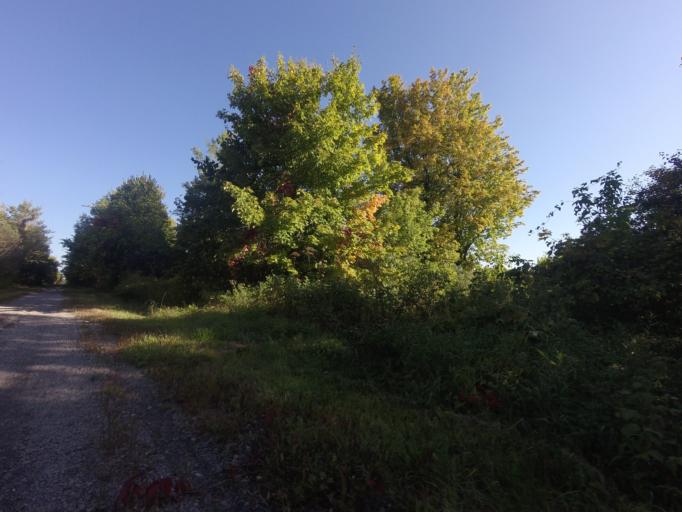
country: CA
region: Ontario
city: Hawkesbury
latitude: 45.5222
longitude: -74.5380
